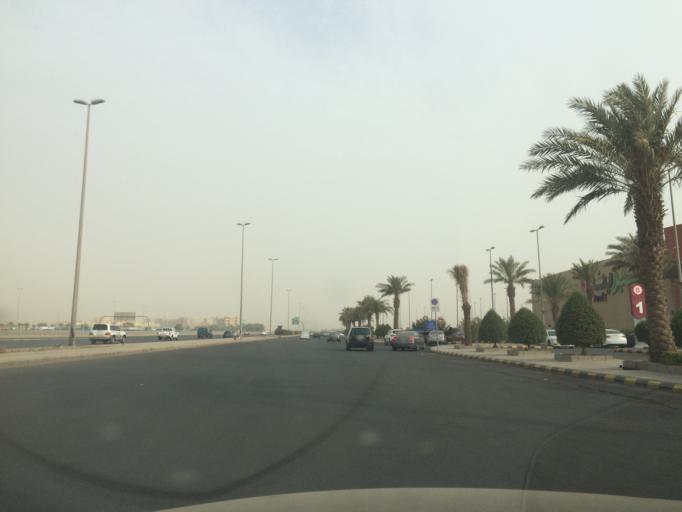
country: SA
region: Makkah
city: Jeddah
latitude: 21.5073
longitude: 39.2196
